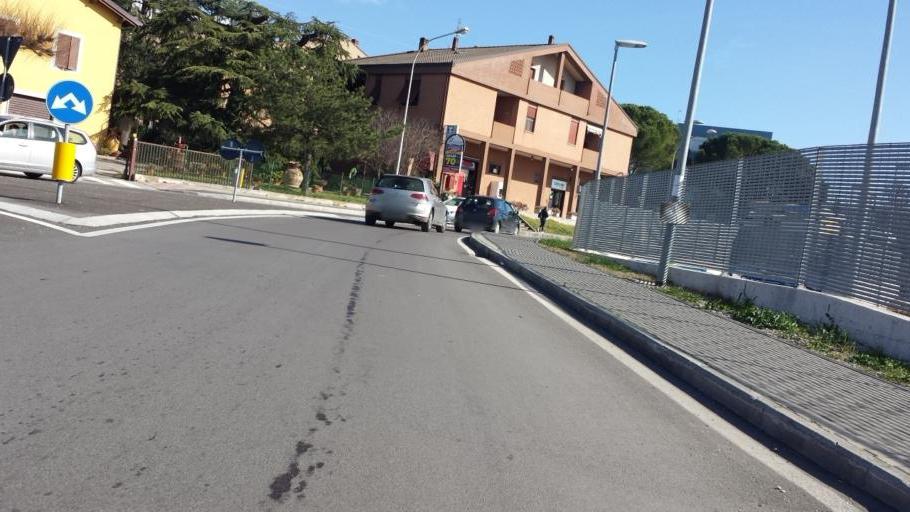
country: IT
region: Umbria
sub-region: Provincia di Terni
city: Terni
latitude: 42.5886
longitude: 12.6025
